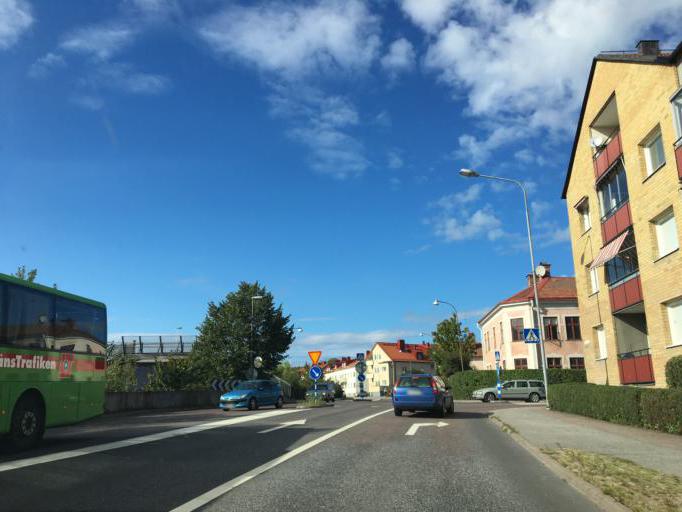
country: SE
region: Soedermanland
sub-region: Nykopings Kommun
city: Nykoping
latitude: 58.7528
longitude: 16.9983
